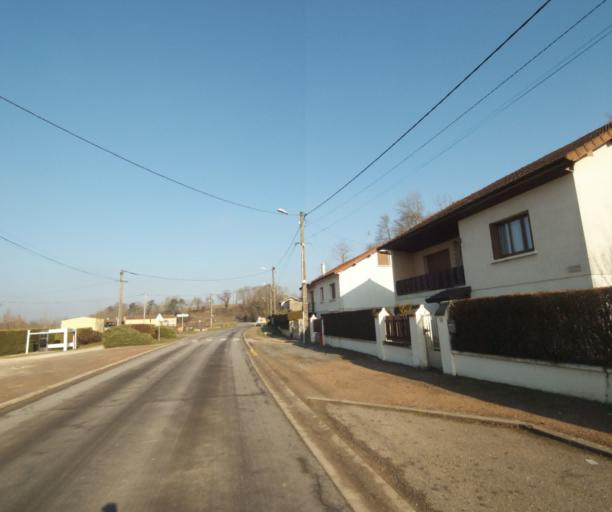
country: FR
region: Champagne-Ardenne
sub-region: Departement de la Haute-Marne
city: Wassy
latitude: 48.4764
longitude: 4.9705
